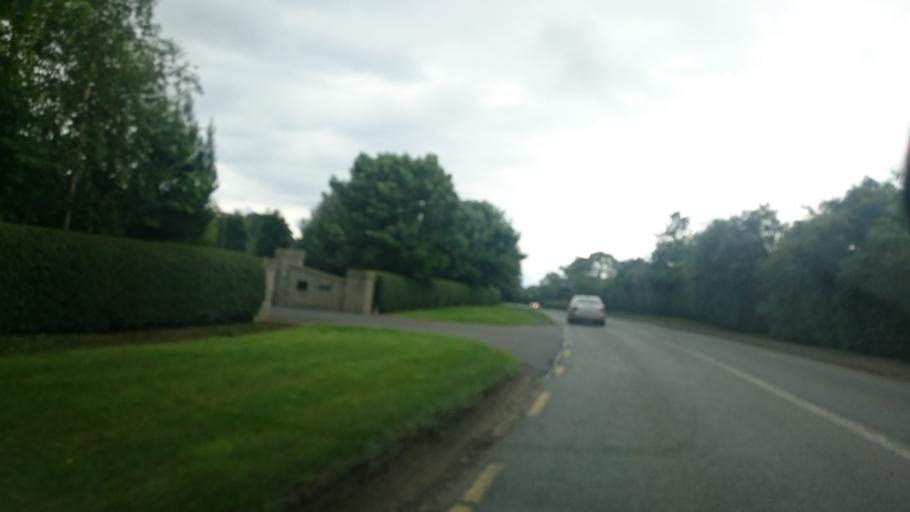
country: IE
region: Leinster
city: Lusk
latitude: 53.5165
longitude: -6.1720
